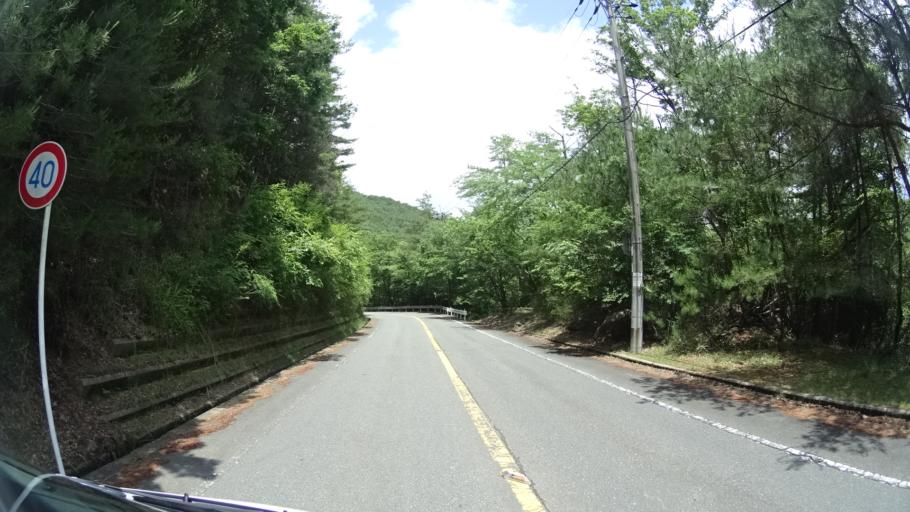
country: JP
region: Kyoto
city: Kameoka
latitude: 35.0334
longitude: 135.4027
